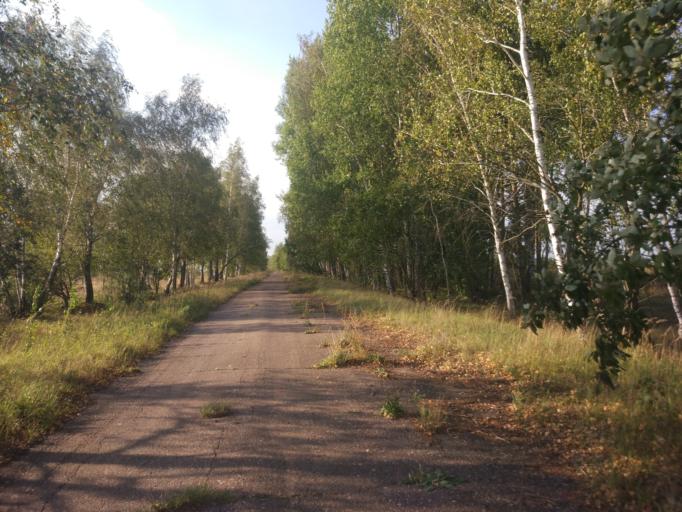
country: RU
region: Brjansk
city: Vyshkov
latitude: 52.6598
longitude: 31.5779
